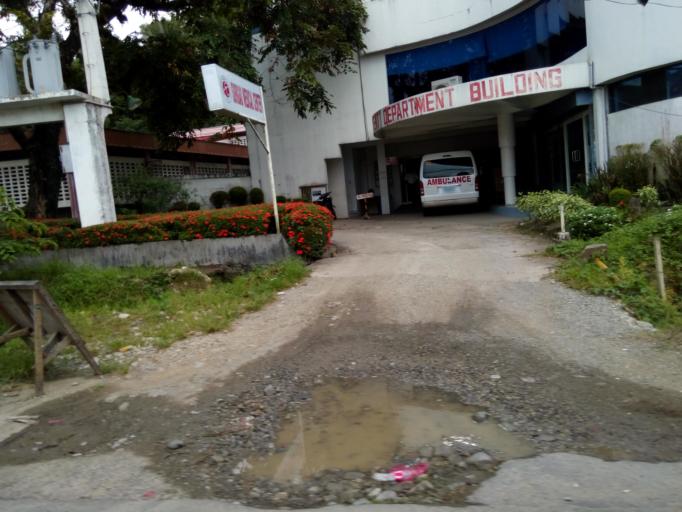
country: PH
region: Caraga
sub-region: Province of Surigao del Norte
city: Surigao
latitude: 9.7812
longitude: 125.4861
